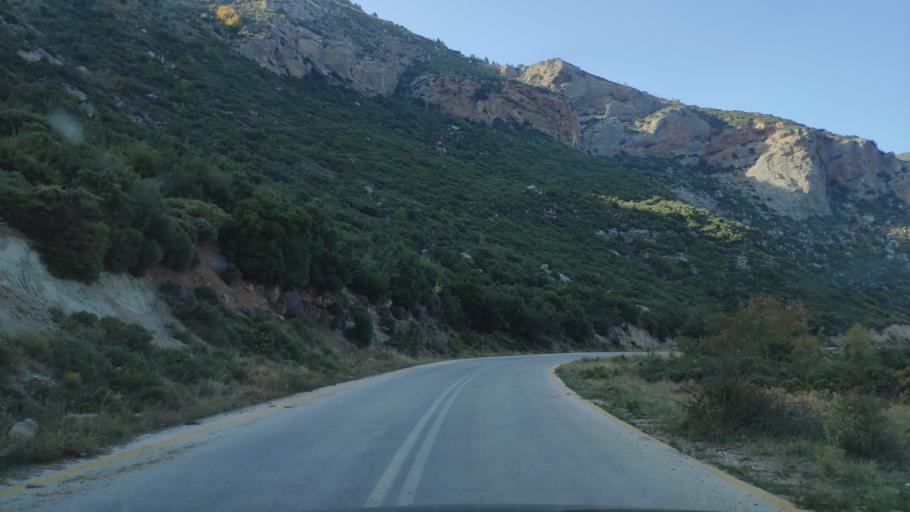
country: GR
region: West Greece
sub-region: Nomos Achaias
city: Aiyira
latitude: 38.0602
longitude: 22.3784
